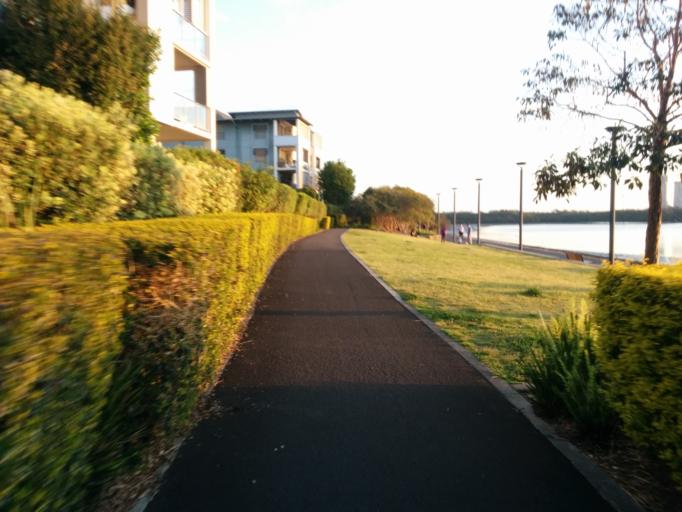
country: AU
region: New South Wales
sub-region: Canada Bay
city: Rhodes
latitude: -33.8333
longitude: 151.0832
